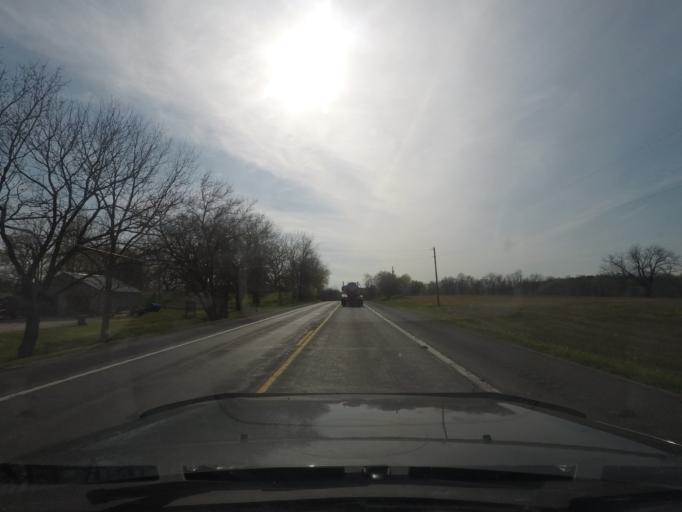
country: US
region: Indiana
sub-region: Saint Joseph County
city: New Carlisle
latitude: 41.7980
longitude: -86.4764
